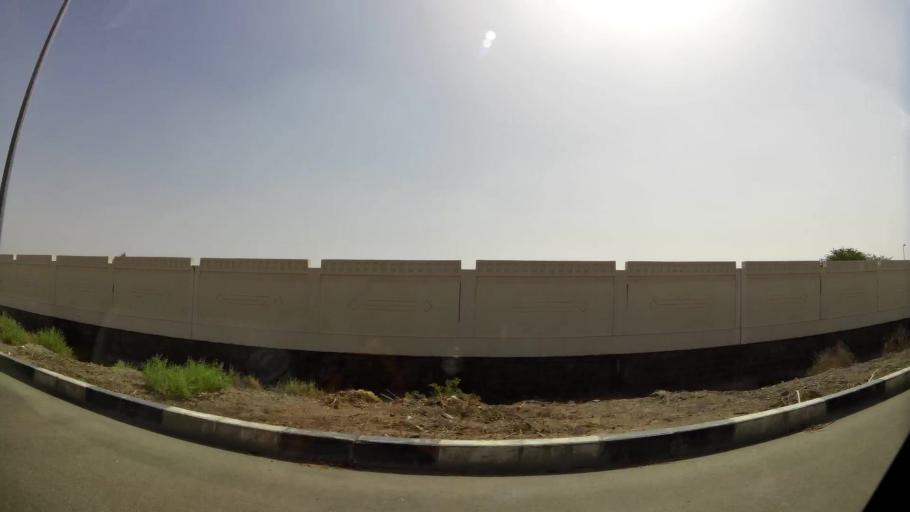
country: AE
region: Abu Dhabi
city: Al Ain
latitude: 24.2339
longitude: 55.6889
